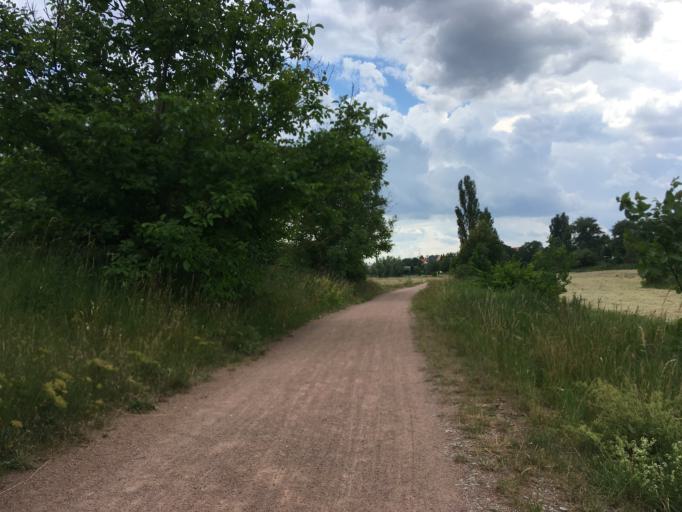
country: DE
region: Saxony-Anhalt
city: Bernburg
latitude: 51.7859
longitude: 11.7698
